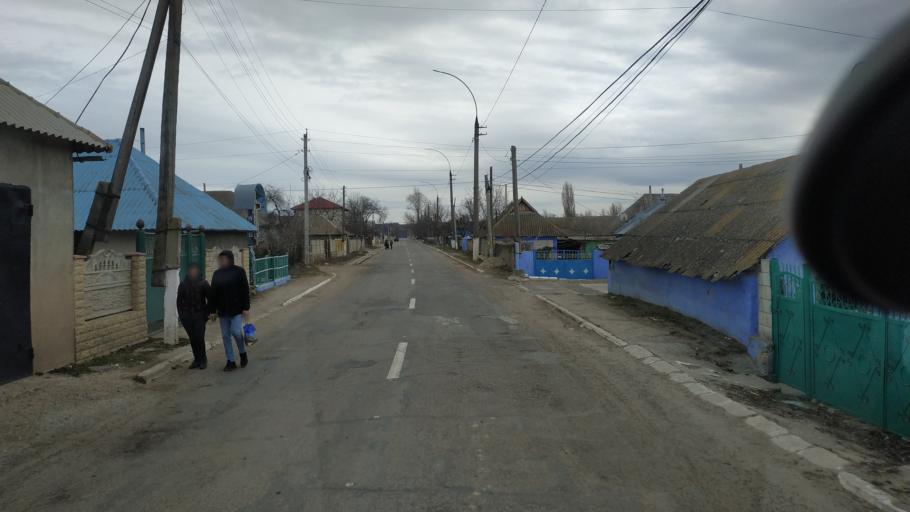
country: MD
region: Telenesti
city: Cocieri
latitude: 47.3430
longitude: 29.1156
